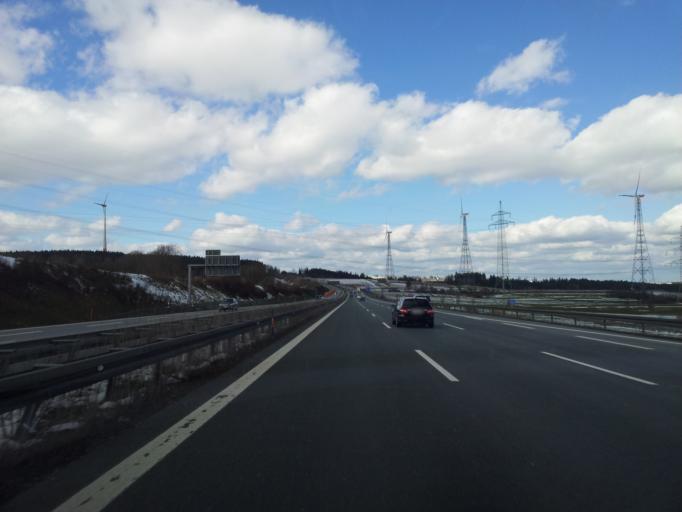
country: DE
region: Bavaria
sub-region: Upper Franconia
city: Munchberg
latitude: 50.2088
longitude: 11.7787
